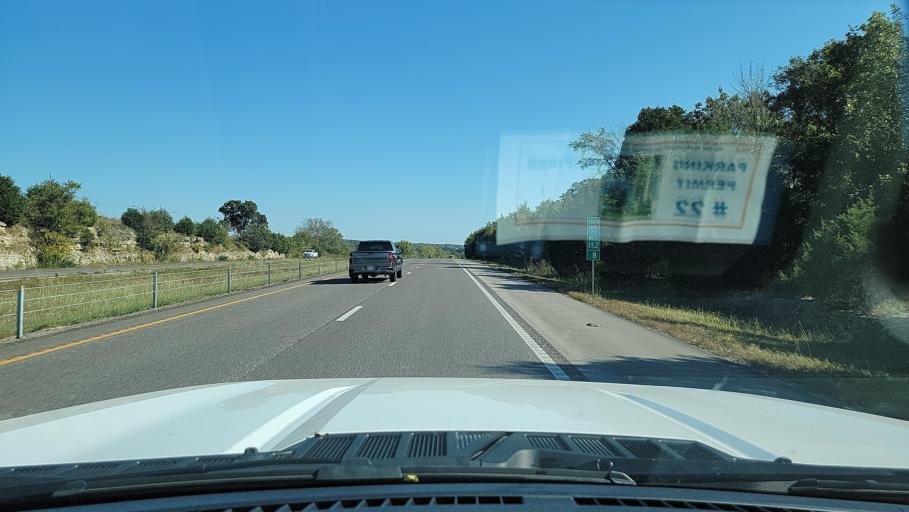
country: US
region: Missouri
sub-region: Sainte Genevieve County
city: Sainte Genevieve
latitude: 37.9572
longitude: -90.1600
